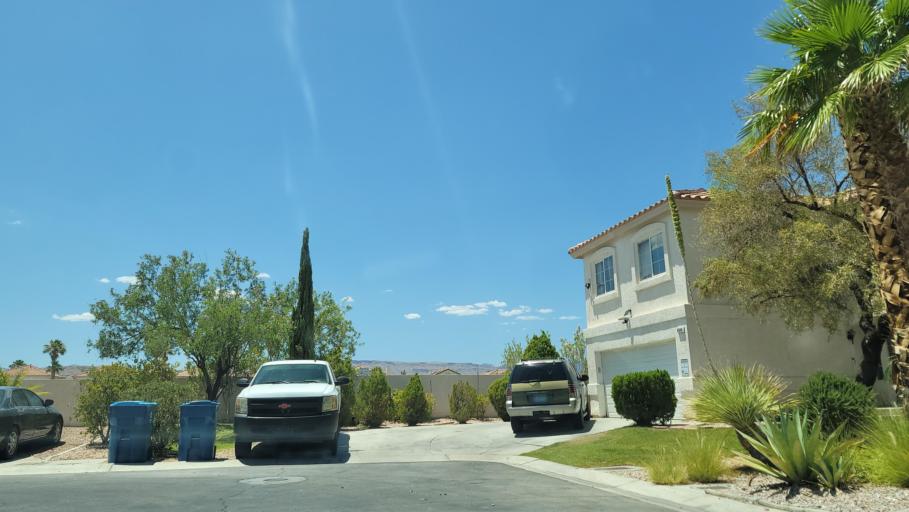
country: US
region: Nevada
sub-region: Clark County
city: Spring Valley
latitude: 36.0789
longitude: -115.2733
